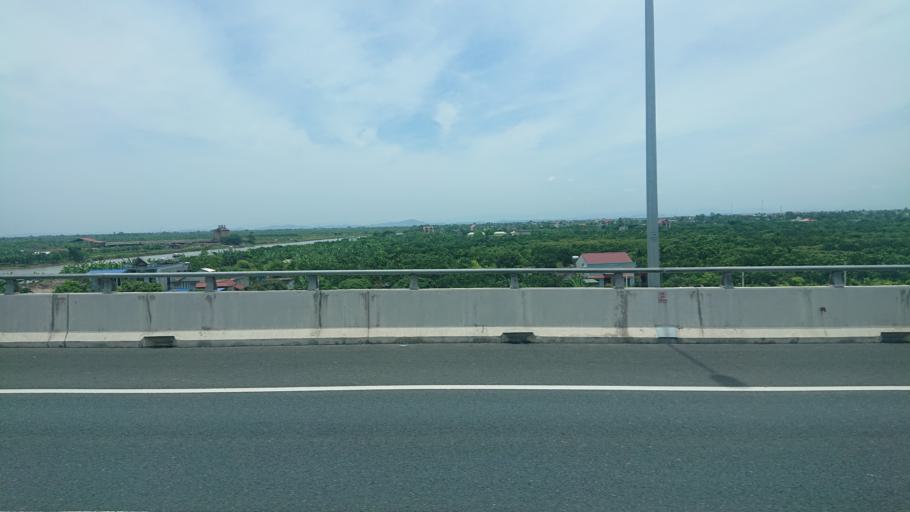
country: VN
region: Hai Duong
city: Tu Ky
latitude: 20.8322
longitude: 106.4441
